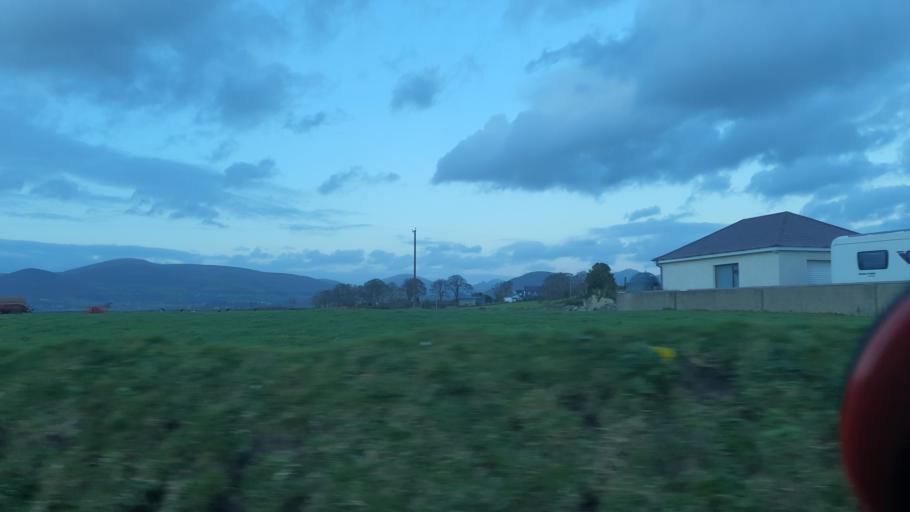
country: IE
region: Leinster
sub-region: Lu
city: Carlingford
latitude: 54.0397
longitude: -6.1009
